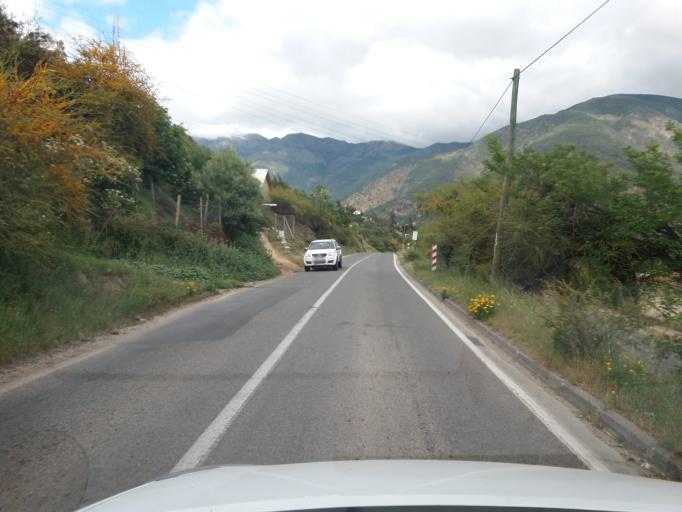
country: CL
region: Valparaiso
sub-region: Provincia de Marga Marga
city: Limache
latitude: -33.0516
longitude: -71.1029
